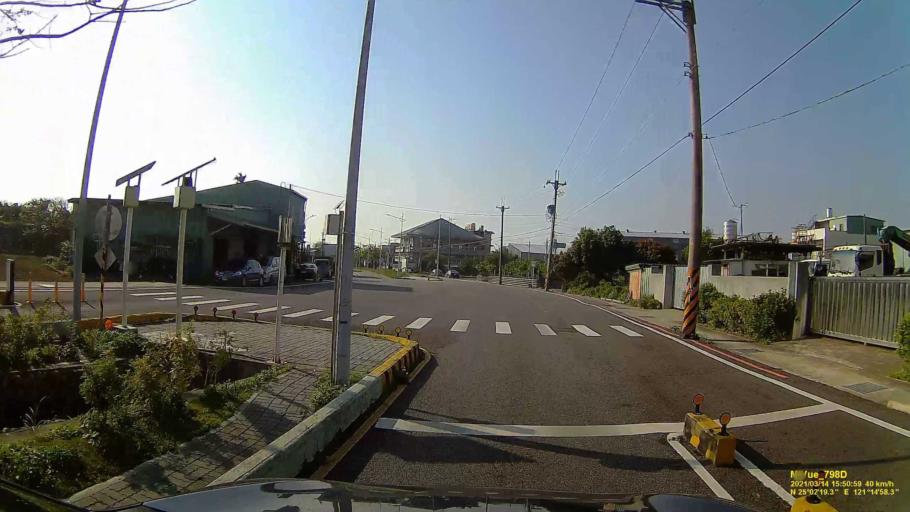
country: TW
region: Taiwan
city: Taoyuan City
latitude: 25.0388
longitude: 121.2493
